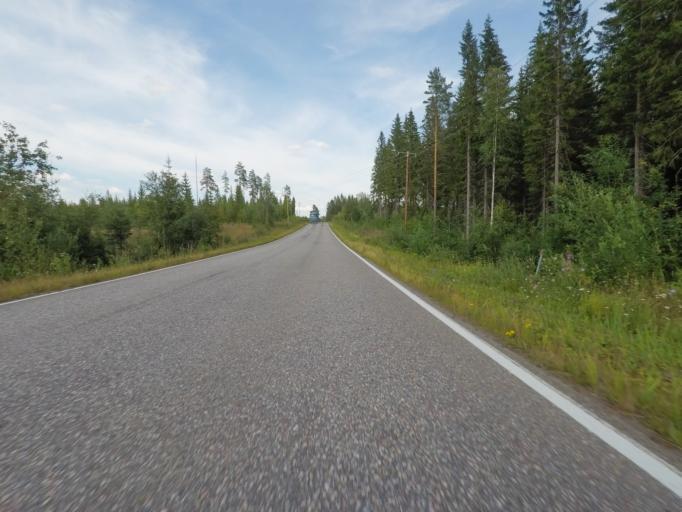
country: FI
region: Southern Savonia
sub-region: Savonlinna
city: Sulkava
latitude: 61.7490
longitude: 28.2047
